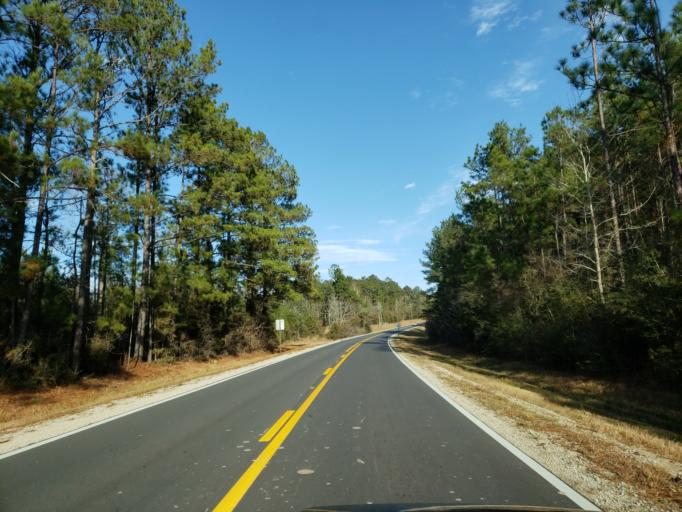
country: US
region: Mississippi
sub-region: Wayne County
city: Belmont
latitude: 31.4309
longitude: -88.4855
